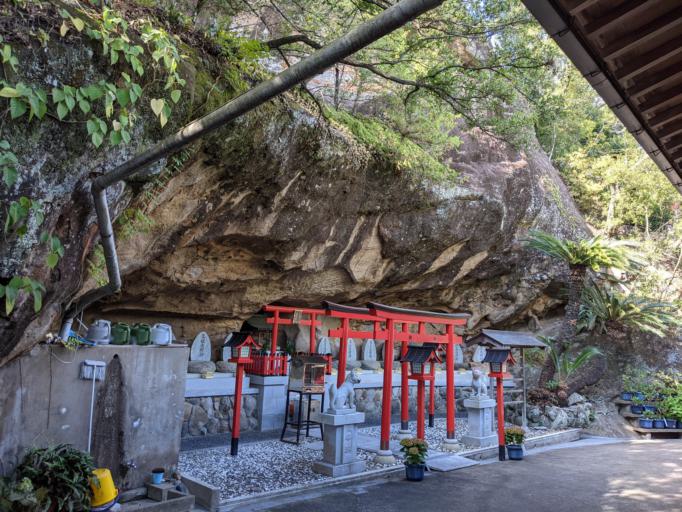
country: JP
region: Wakayama
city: Tanabe
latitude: 33.7140
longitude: 135.4282
